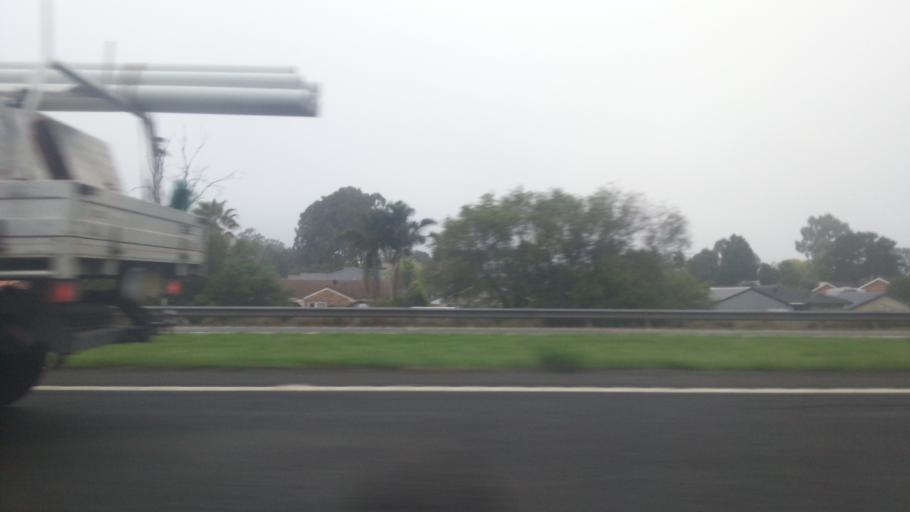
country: AU
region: New South Wales
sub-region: Camden
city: Narellan Vale
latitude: -34.0547
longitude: 150.7358
